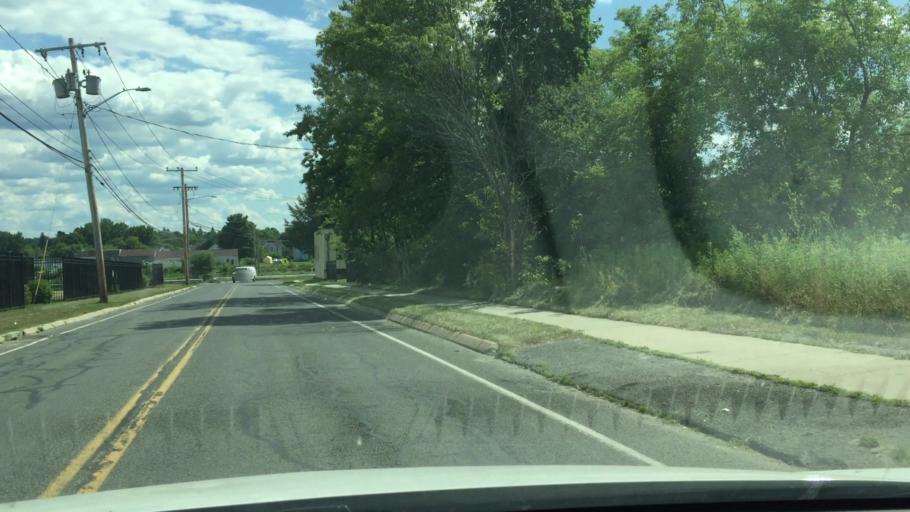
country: US
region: Massachusetts
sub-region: Berkshire County
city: Pittsfield
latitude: 42.4528
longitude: -73.2421
